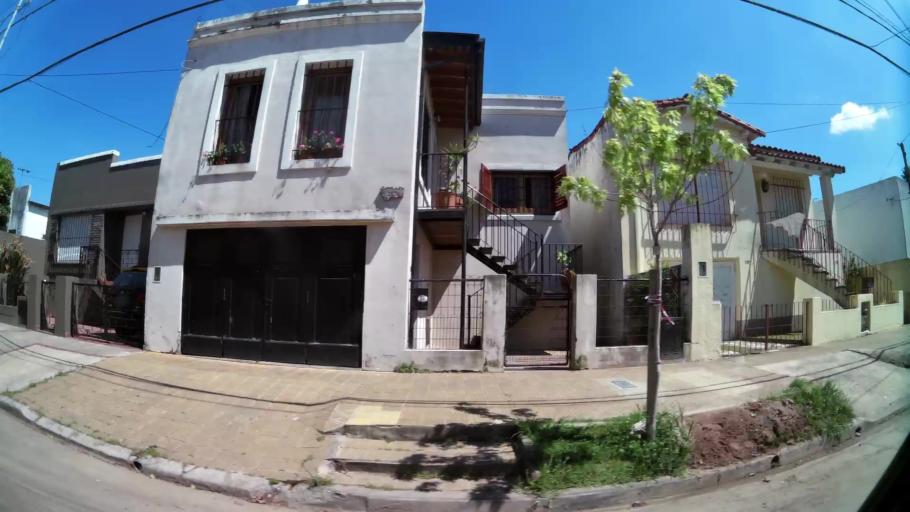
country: AR
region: Buenos Aires
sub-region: Partido de Tigre
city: Tigre
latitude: -34.4275
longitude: -58.5700
